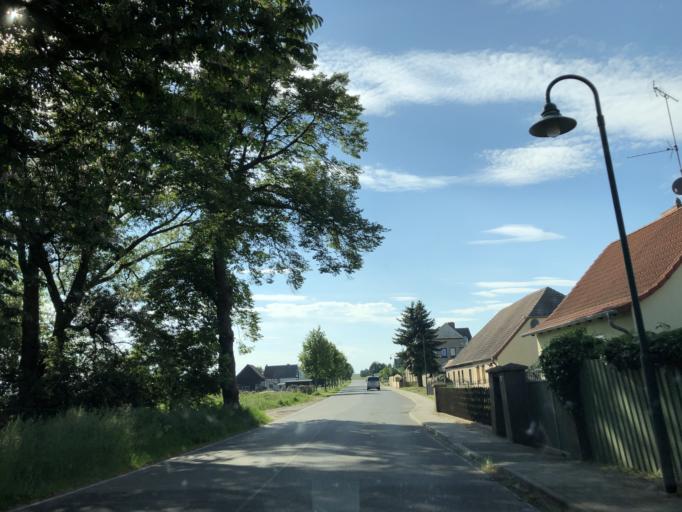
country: DE
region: Brandenburg
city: Angermunde
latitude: 53.0874
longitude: 13.9450
